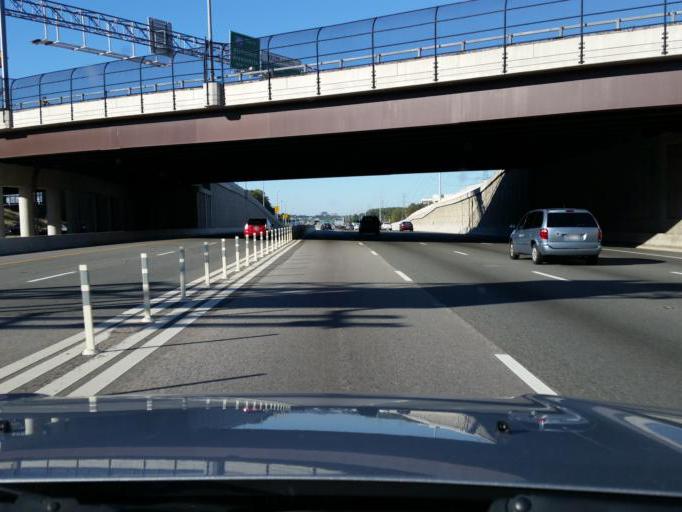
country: US
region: Virginia
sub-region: Fairfax County
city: Merrifield
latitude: 38.8532
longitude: -77.2198
